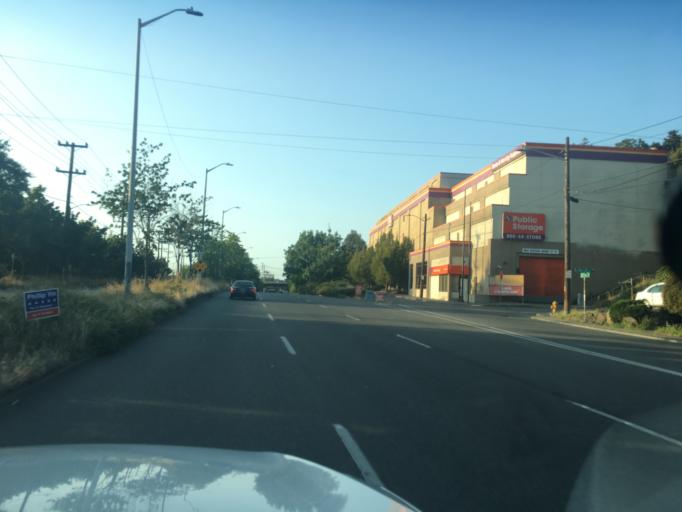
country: US
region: Washington
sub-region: King County
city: Seattle
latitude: 47.6461
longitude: -122.3763
